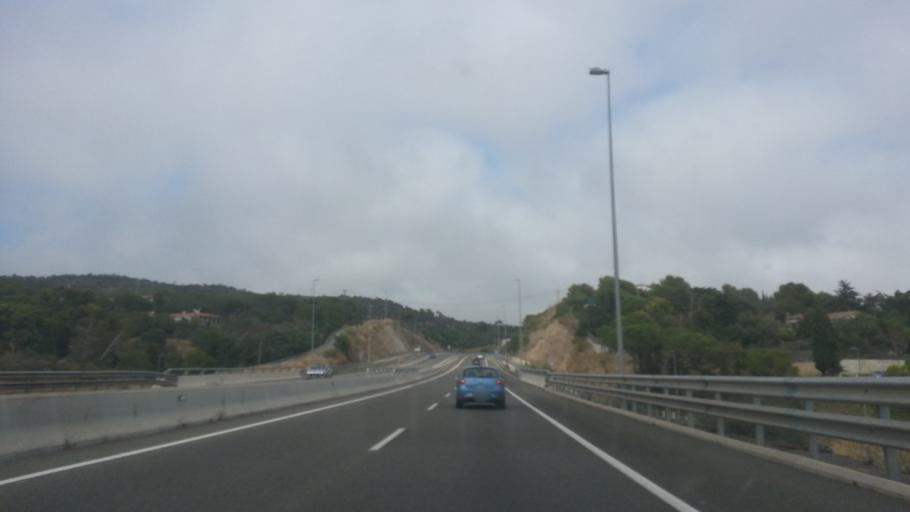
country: ES
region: Catalonia
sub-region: Provincia de Girona
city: Castell-Platja d'Aro
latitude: 41.8263
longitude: 3.0605
